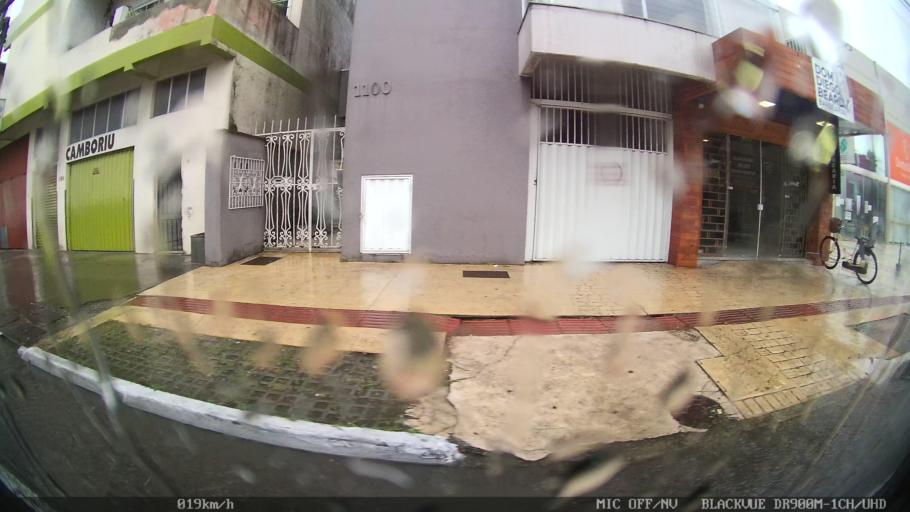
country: BR
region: Santa Catarina
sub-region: Balneario Camboriu
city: Balneario Camboriu
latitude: -27.0011
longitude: -48.6368
